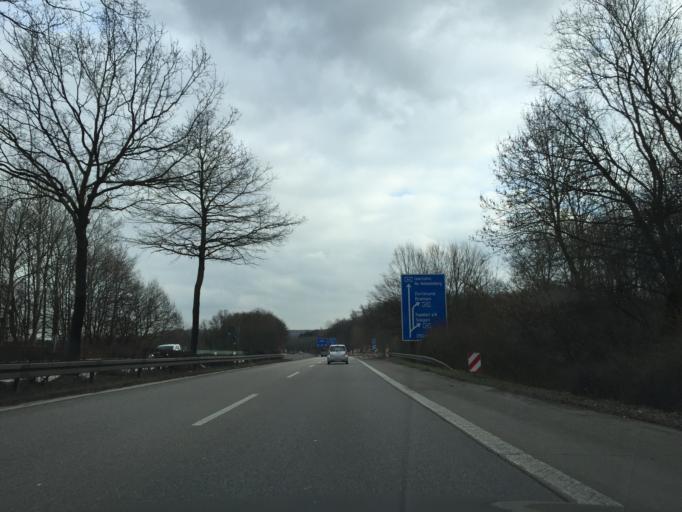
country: DE
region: North Rhine-Westphalia
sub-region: Regierungsbezirk Arnsberg
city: Hagen
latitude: 51.3732
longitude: 7.5050
